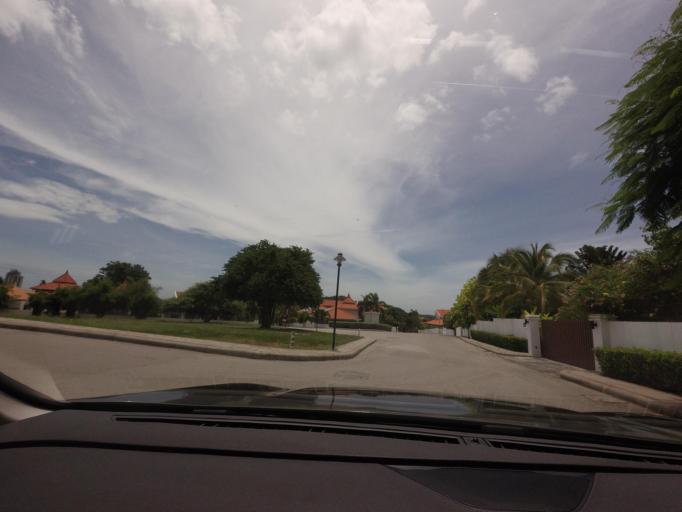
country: TH
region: Prachuap Khiri Khan
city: Hua Hin
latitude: 12.5152
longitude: 99.9580
